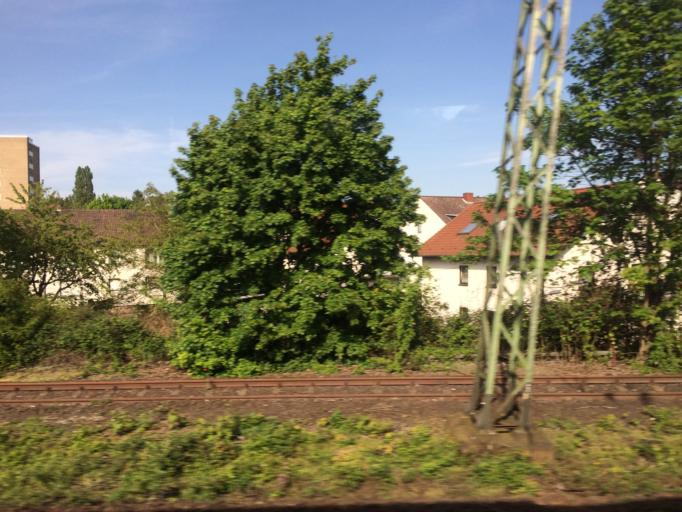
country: DE
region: North Rhine-Westphalia
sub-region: Regierungsbezirk Koln
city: Bonn
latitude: 50.7301
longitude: 7.1334
